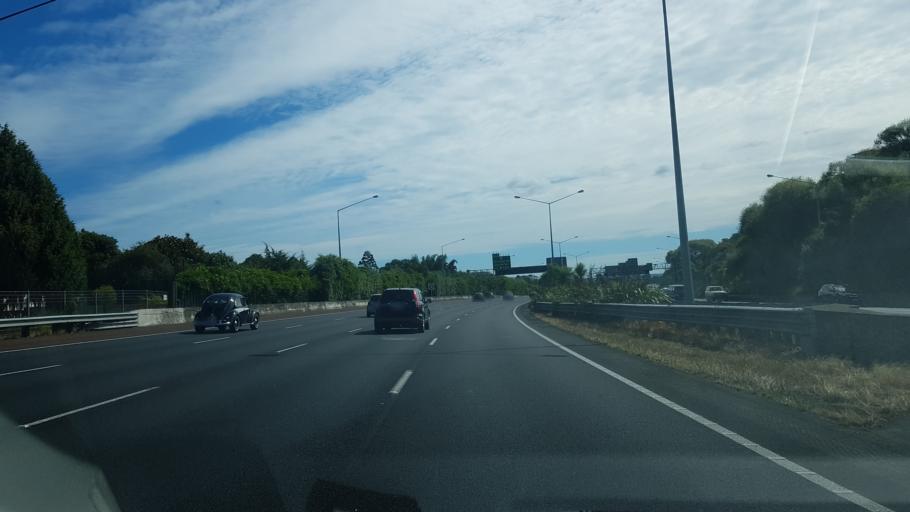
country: NZ
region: Auckland
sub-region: Auckland
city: Rosebank
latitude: -36.8700
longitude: 174.6737
